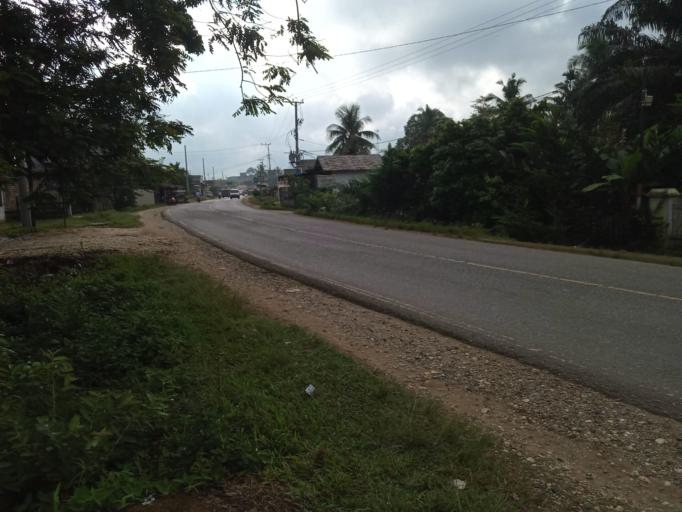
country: ID
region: Jambi
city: Muara Tembesi
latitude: -1.7209
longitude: 103.1328
